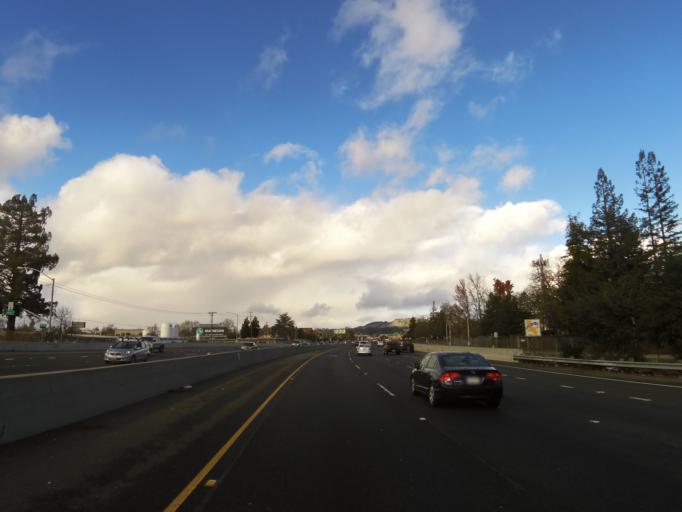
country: US
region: California
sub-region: Sonoma County
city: Santa Rosa
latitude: 38.4498
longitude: -122.7260
